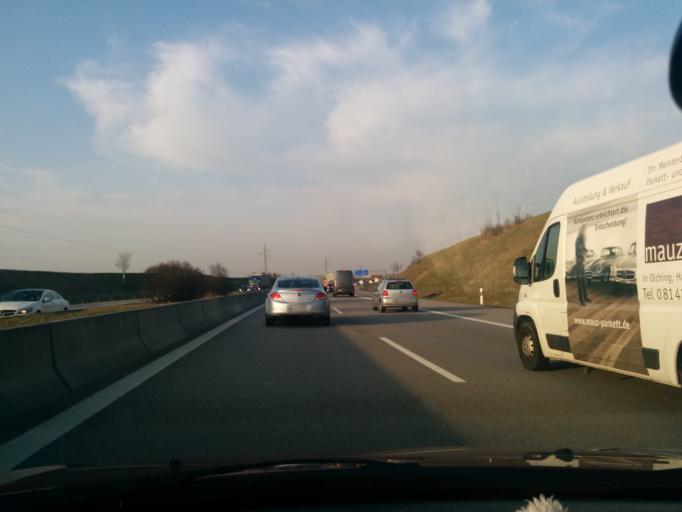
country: DE
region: Bavaria
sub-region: Upper Bavaria
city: Germering
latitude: 48.1515
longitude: 11.3953
